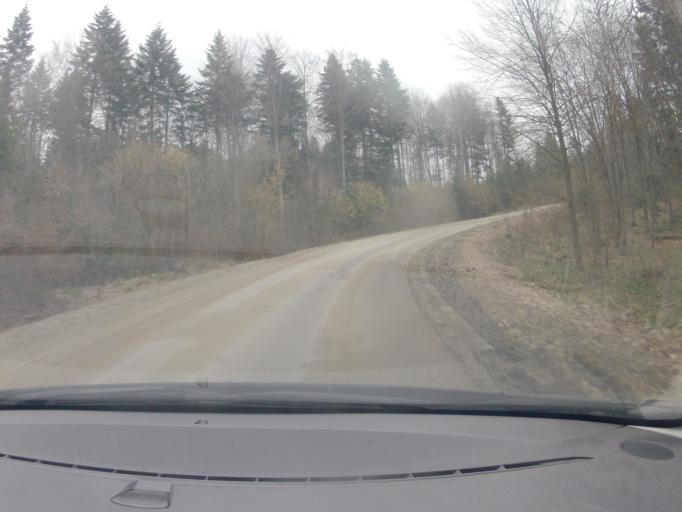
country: PL
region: Subcarpathian Voivodeship
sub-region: Powiat krosnienski
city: Dukla
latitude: 49.5010
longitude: 21.6107
